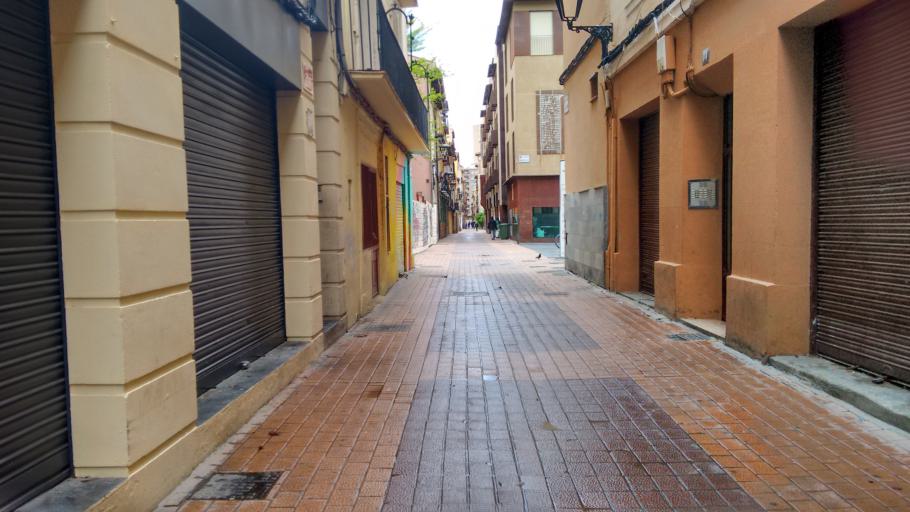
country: ES
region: Aragon
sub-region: Provincia de Zaragoza
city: Zaragoza
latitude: 41.6566
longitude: -0.8850
